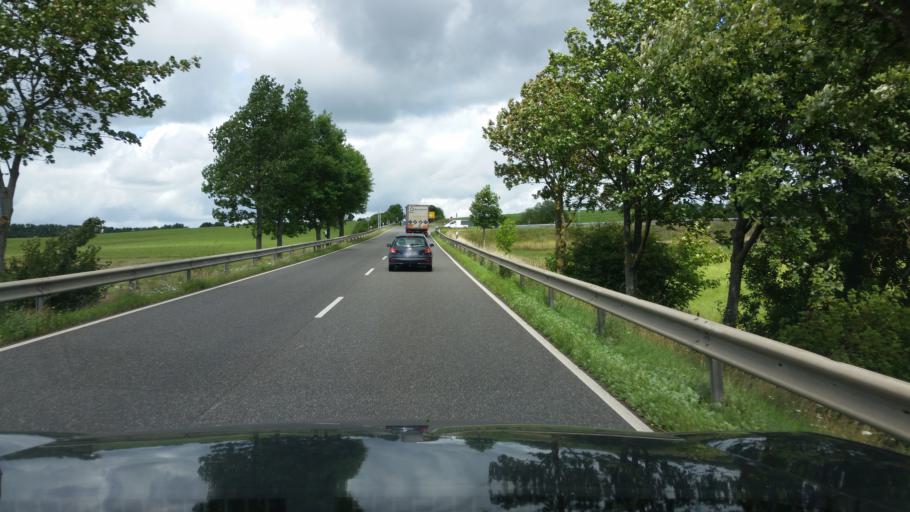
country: DE
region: North Rhine-Westphalia
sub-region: Regierungsbezirk Koln
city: Blankenheim
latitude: 50.4601
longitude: 6.7003
